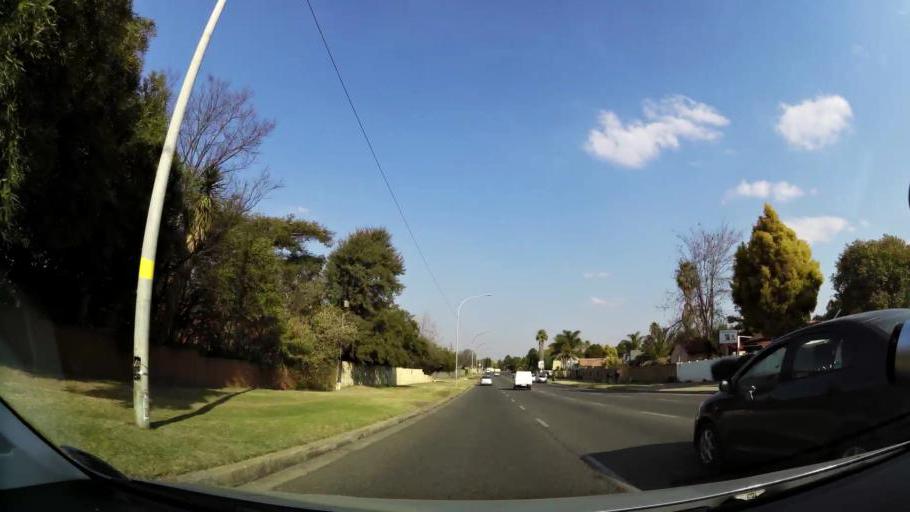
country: ZA
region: Gauteng
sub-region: City of Johannesburg Metropolitan Municipality
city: Modderfontein
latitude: -26.0747
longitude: 28.2094
